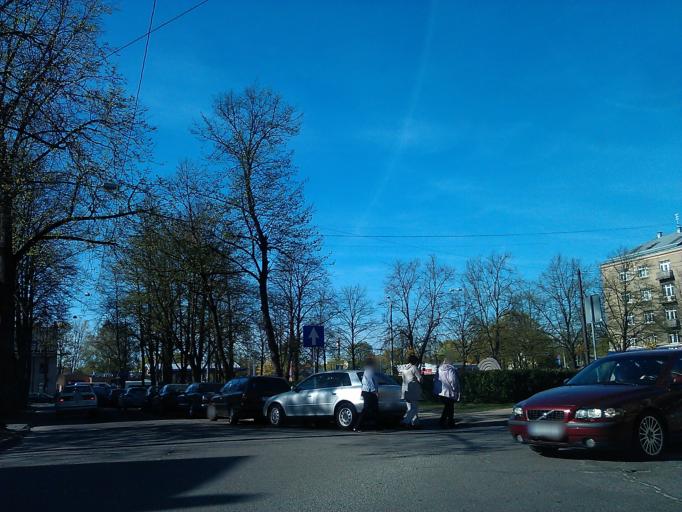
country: LV
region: Riga
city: Jaunciems
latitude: 56.9778
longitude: 24.1852
